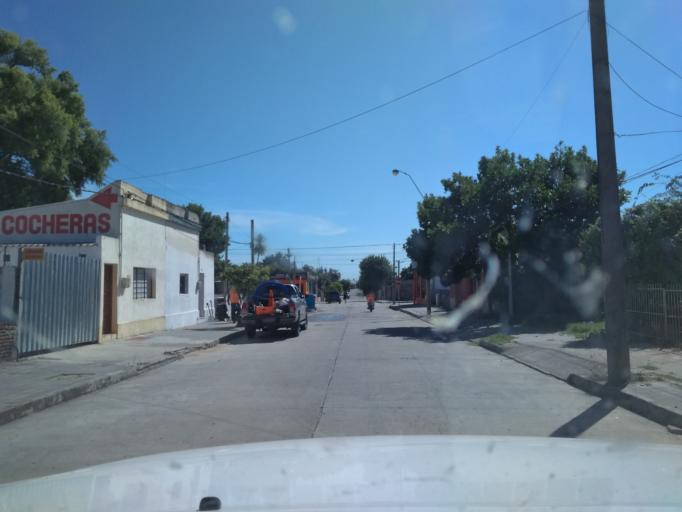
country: UY
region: Florida
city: Florida
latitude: -34.0968
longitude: -56.2109
